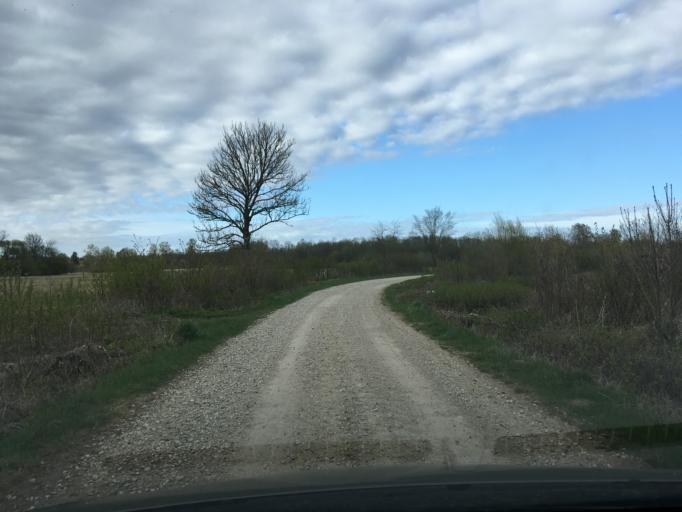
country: EE
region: Laeaene
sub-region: Lihula vald
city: Lihula
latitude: 58.5771
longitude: 23.7234
